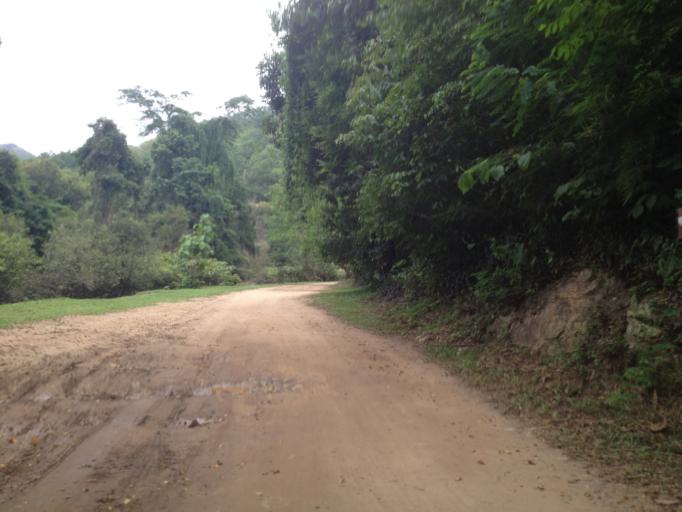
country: TH
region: Chiang Mai
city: Hang Dong
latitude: 18.7202
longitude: 98.8228
